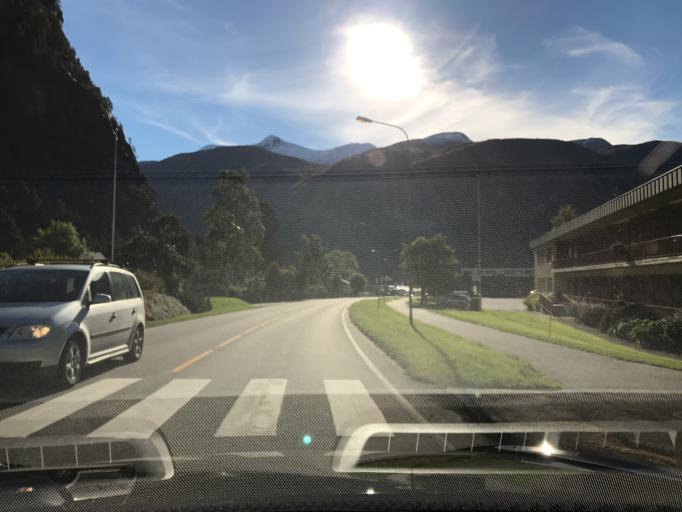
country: NO
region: More og Romsdal
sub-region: Norddal
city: Valldal
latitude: 62.3004
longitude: 7.2614
